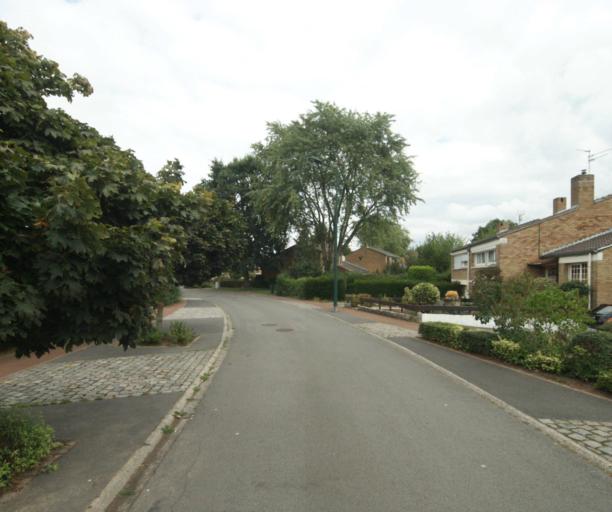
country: FR
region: Nord-Pas-de-Calais
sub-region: Departement du Nord
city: Villeneuve-d'Ascq
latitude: 50.6191
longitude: 3.1532
